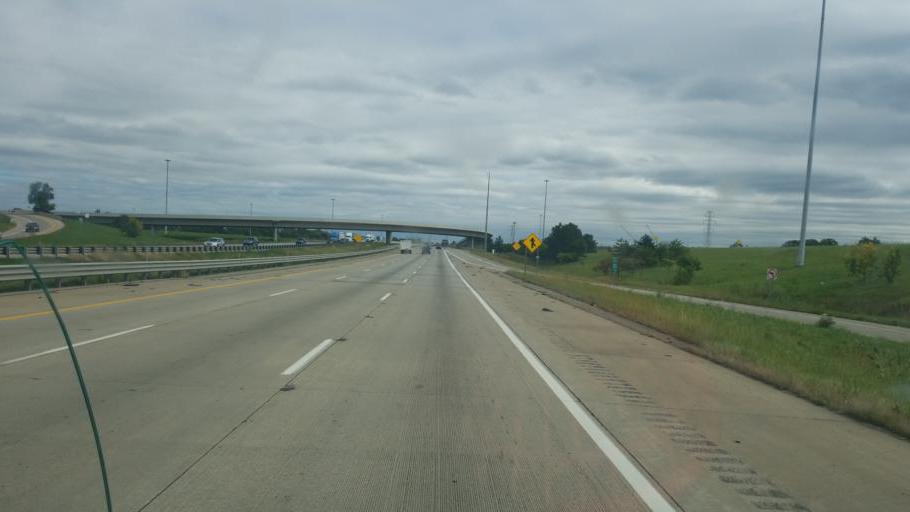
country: US
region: Michigan
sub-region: Wayne County
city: Allen Park
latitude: 42.2664
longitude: -83.2289
